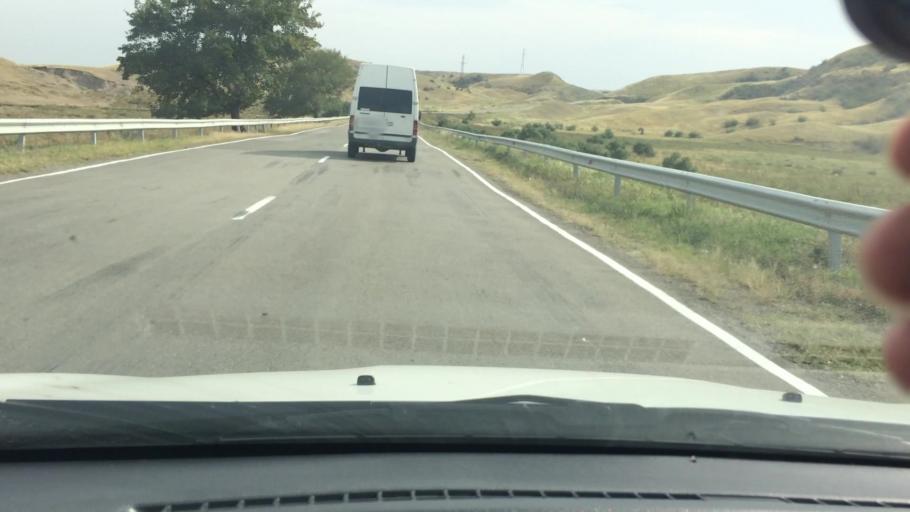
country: GE
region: Kvemo Kartli
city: Rust'avi
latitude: 41.5298
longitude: 44.9856
